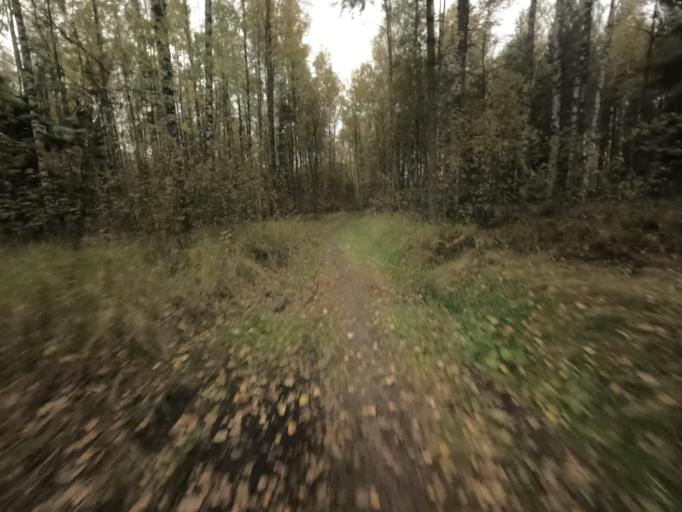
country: RU
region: Leningrad
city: Kirovsk
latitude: 59.8307
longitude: 30.9825
